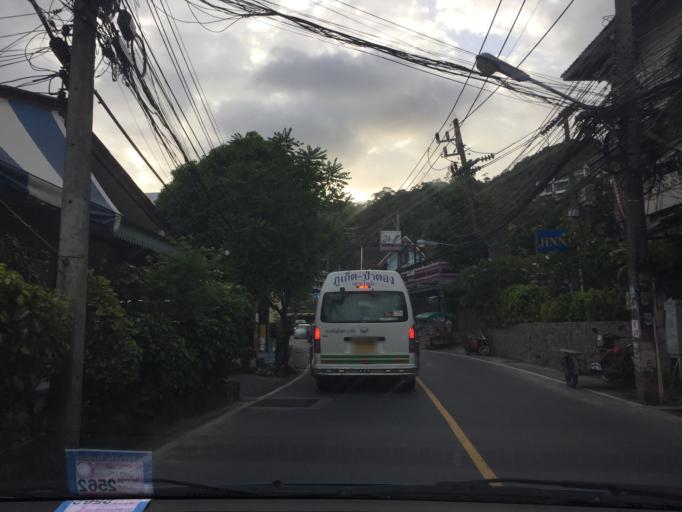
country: TH
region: Phuket
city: Patong
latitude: 7.8967
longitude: 98.3089
